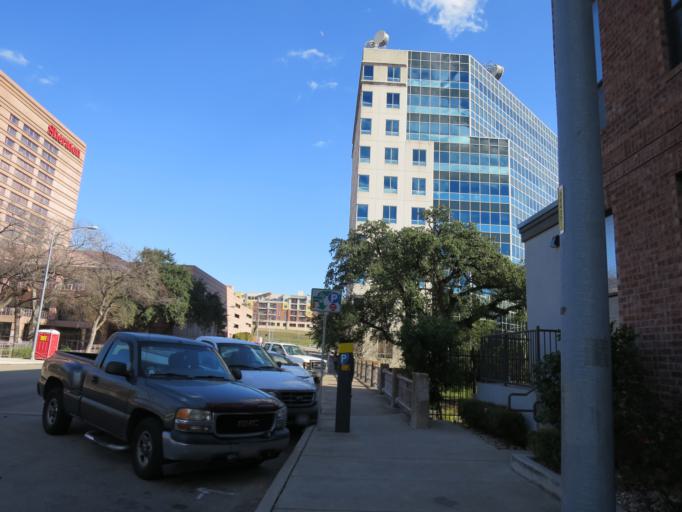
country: US
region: Texas
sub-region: Travis County
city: Austin
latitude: 30.2700
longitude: -97.7355
